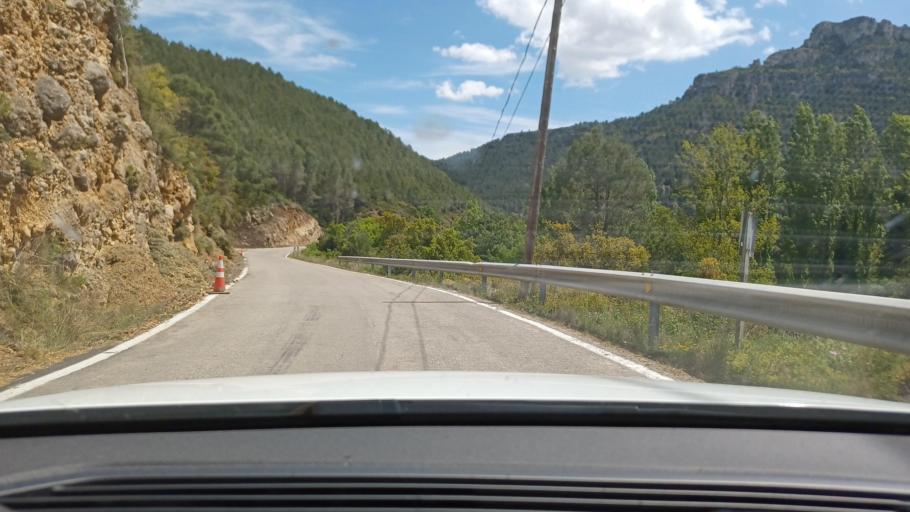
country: ES
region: Valencia
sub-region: Provincia de Castello
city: Rosell
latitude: 40.6704
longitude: 0.2442
